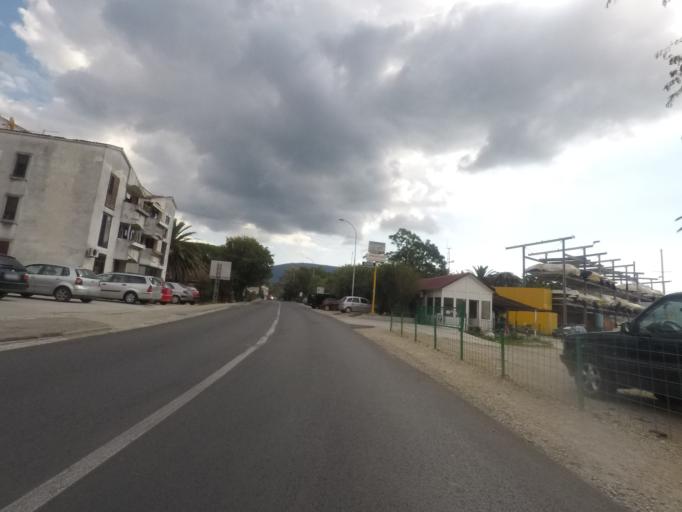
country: ME
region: Herceg Novi
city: Herceg-Novi
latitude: 42.4494
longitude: 18.5738
